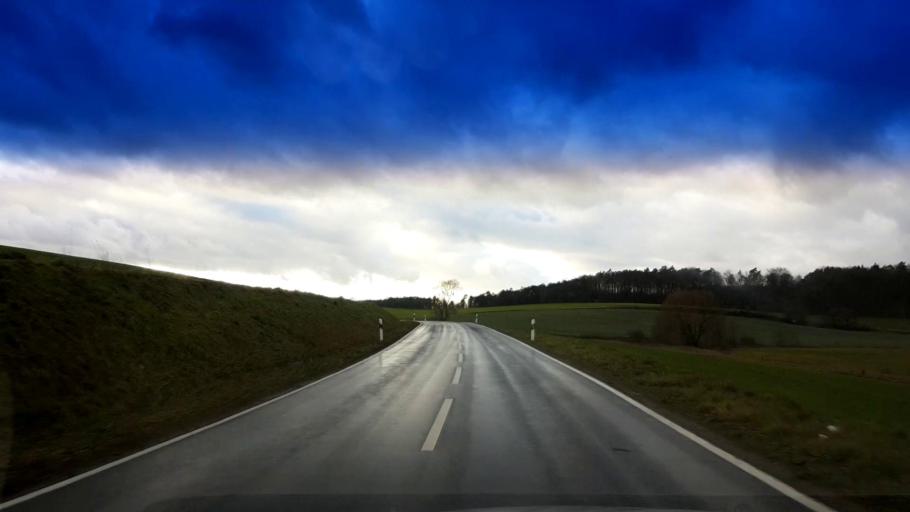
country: DE
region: Bavaria
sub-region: Upper Franconia
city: Lauter
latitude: 50.0029
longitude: 10.7738
